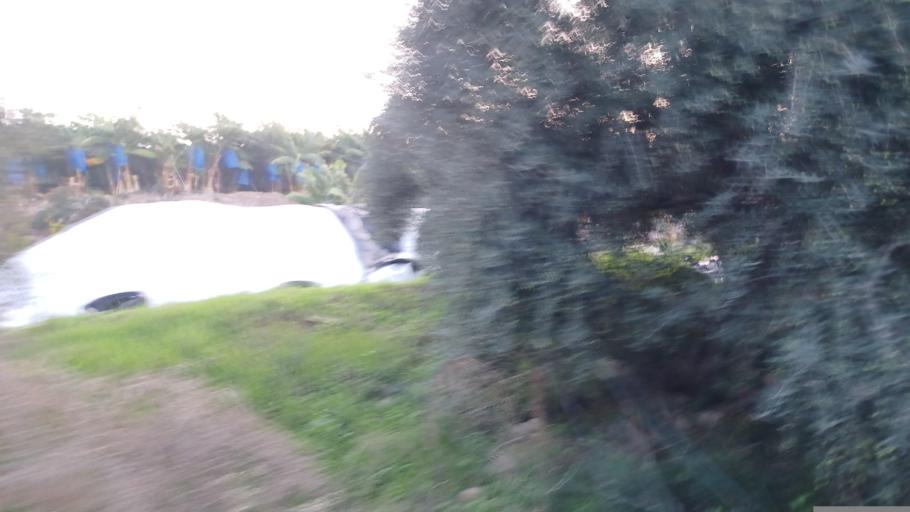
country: CY
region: Pafos
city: Kissonerga
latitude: 34.8424
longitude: 32.4047
